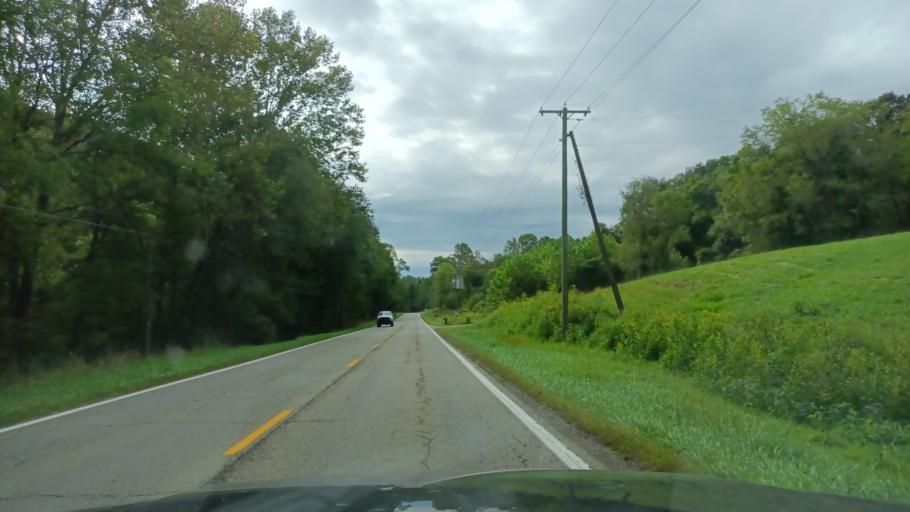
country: US
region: Ohio
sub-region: Vinton County
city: McArthur
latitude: 39.2705
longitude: -82.5758
